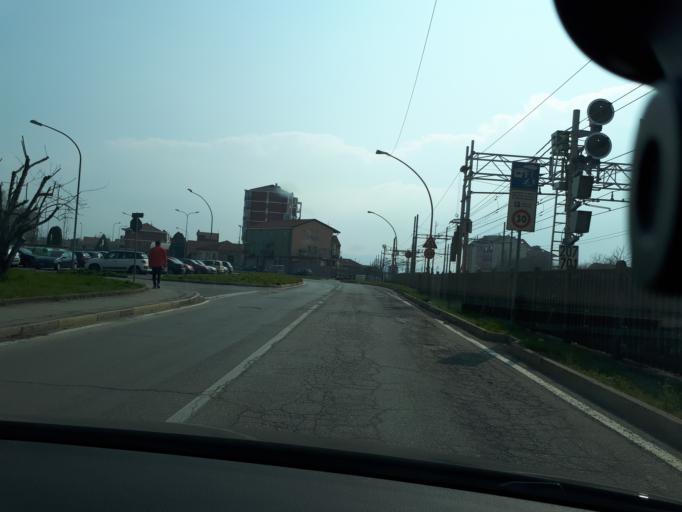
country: IT
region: Piedmont
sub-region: Provincia di Torino
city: Lesna
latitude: 45.0651
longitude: 7.6066
